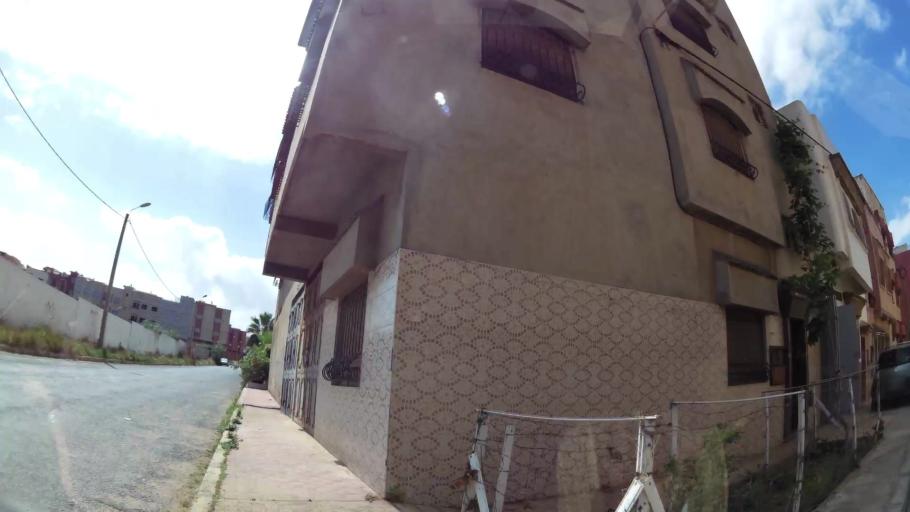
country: MA
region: Rabat-Sale-Zemmour-Zaer
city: Sale
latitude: 34.0721
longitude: -6.7937
